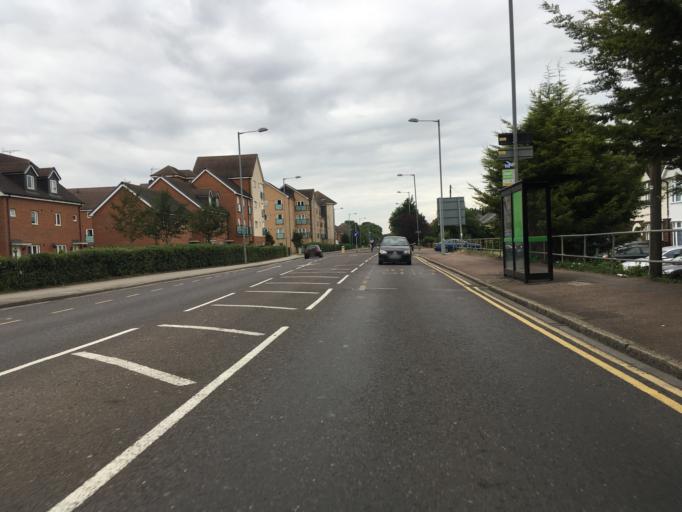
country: GB
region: England
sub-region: Central Bedfordshire
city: Dunstable
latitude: 51.8948
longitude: -0.5333
